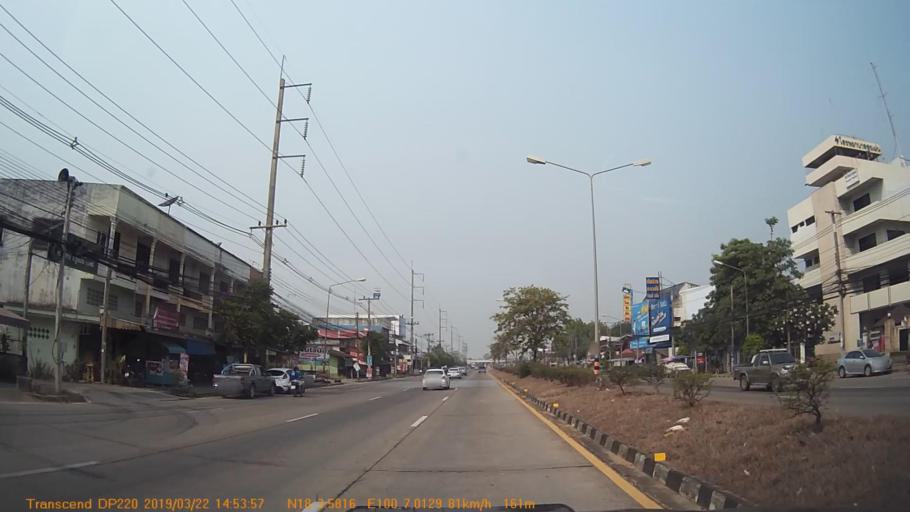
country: TH
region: Phrae
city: Sung Men
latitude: 18.0601
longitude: 100.1171
